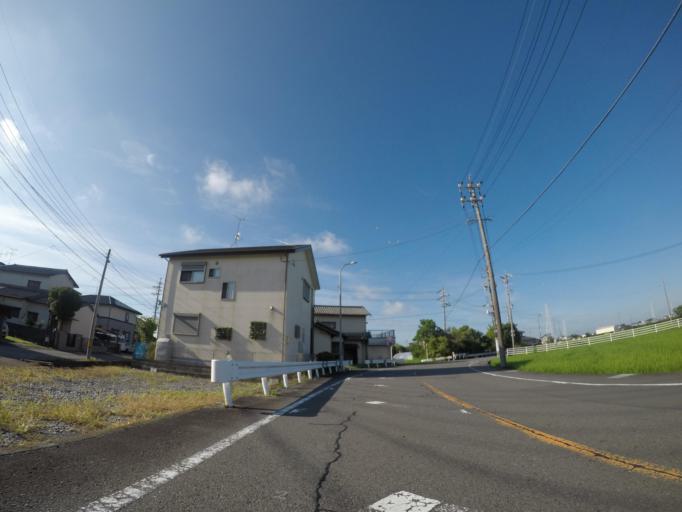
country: JP
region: Shizuoka
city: Yaizu
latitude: 34.8328
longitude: 138.3119
